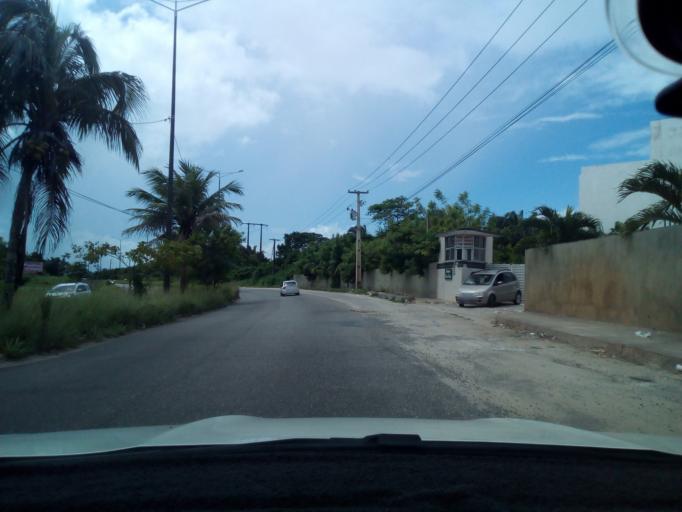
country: BR
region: Paraiba
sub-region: Bayeux
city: Bayeux
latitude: -7.1435
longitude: -34.9061
